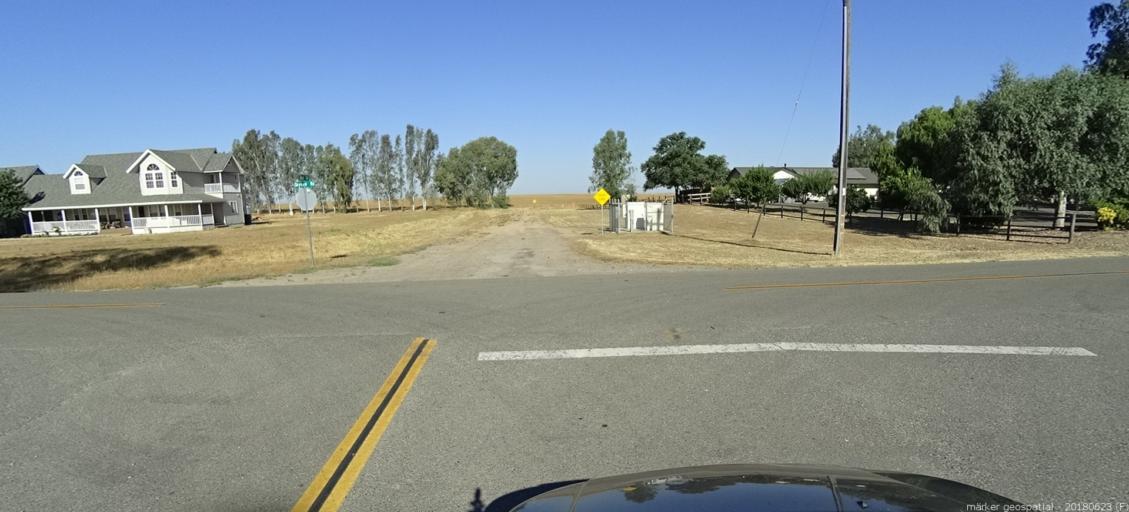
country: US
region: California
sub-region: Madera County
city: Bonadelle Ranchos-Madera Ranchos
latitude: 36.9595
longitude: -119.8014
